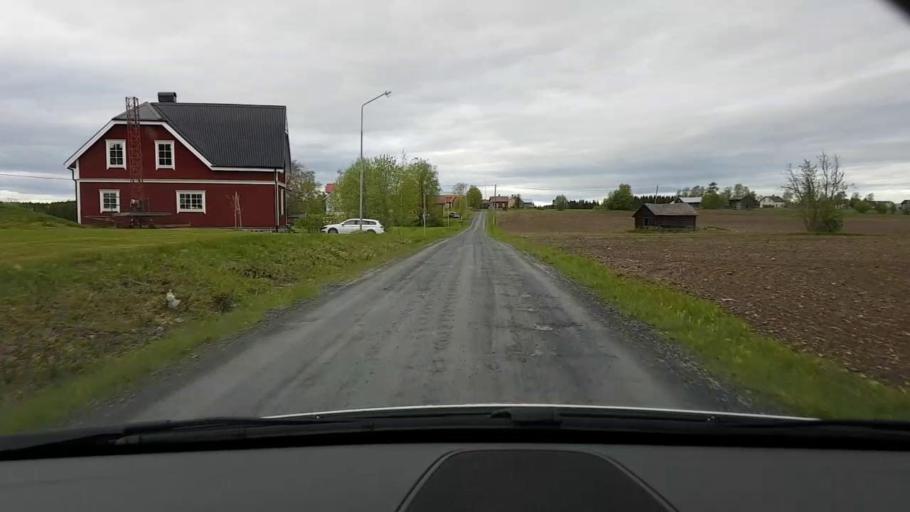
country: SE
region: Jaemtland
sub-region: Krokoms Kommun
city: Valla
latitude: 63.3041
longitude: 14.0171
